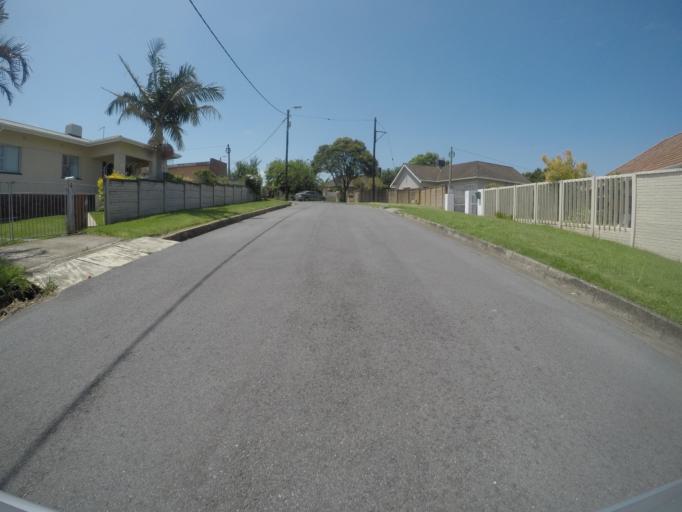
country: ZA
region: Eastern Cape
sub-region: Buffalo City Metropolitan Municipality
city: East London
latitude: -32.9714
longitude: 27.8666
